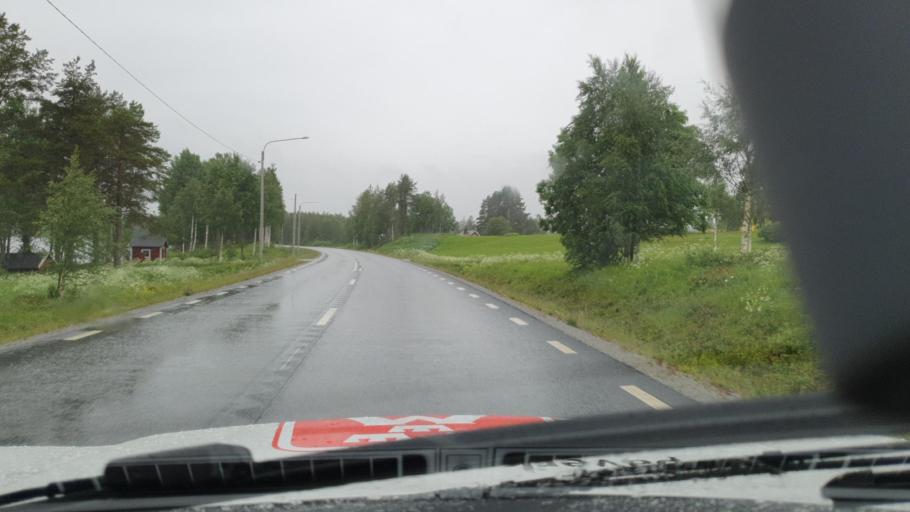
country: SE
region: Vaesterbotten
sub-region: Asele Kommun
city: Insjon
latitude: 64.1406
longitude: 18.0360
